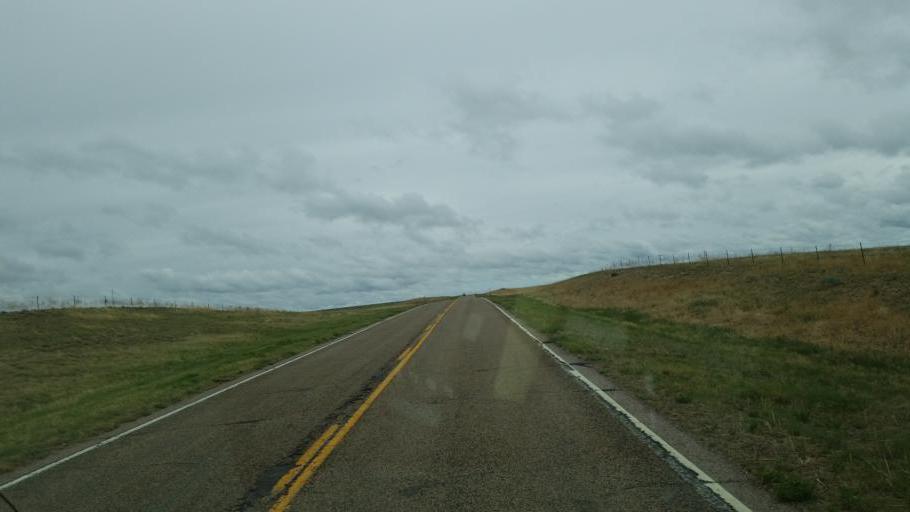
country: US
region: Colorado
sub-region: Lincoln County
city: Hugo
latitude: 38.8503
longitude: -103.4522
